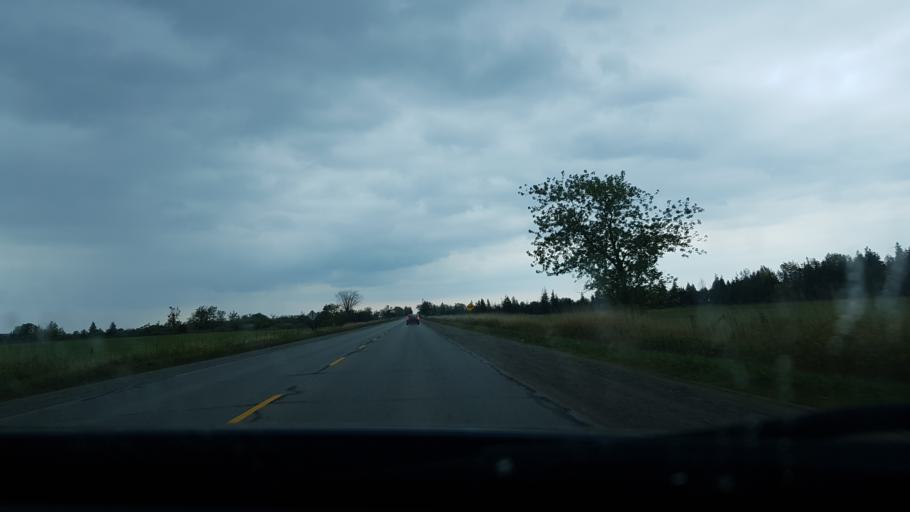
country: CA
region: Ontario
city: Omemee
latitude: 44.3739
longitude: -78.6554
